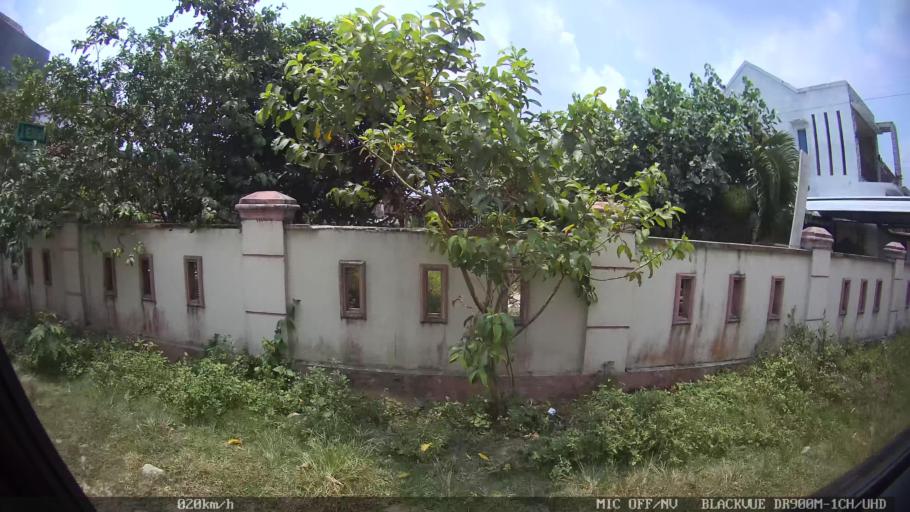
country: ID
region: Lampung
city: Pringsewu
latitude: -5.3513
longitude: 104.9636
